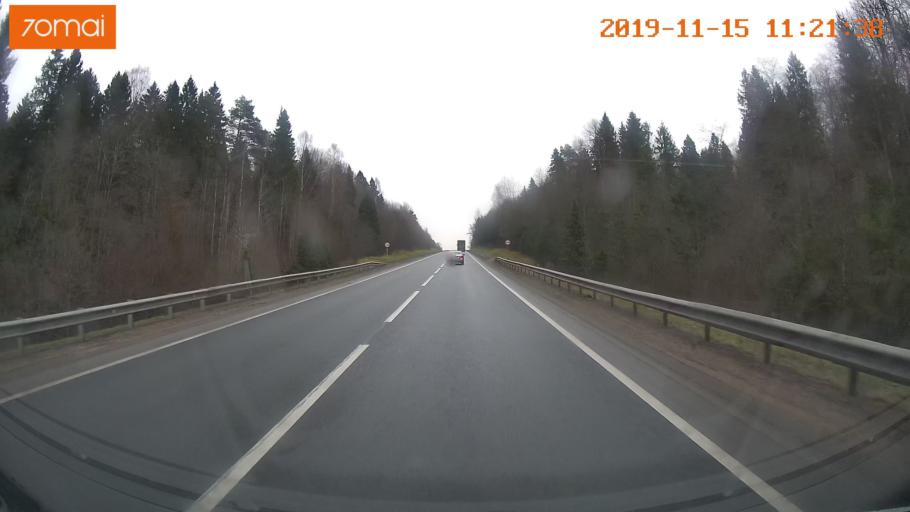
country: RU
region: Vologda
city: Molochnoye
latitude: 59.1451
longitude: 39.3424
